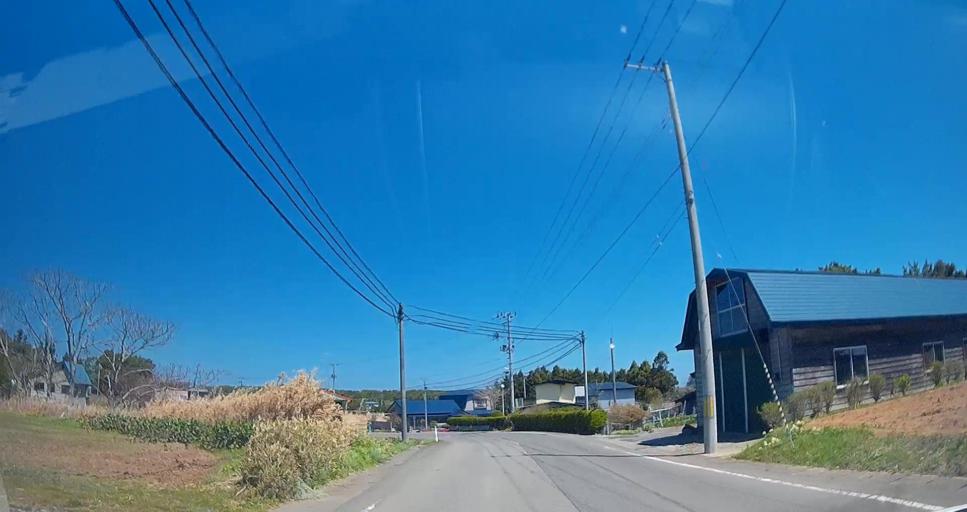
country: JP
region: Aomori
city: Mutsu
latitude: 41.2296
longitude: 141.3974
